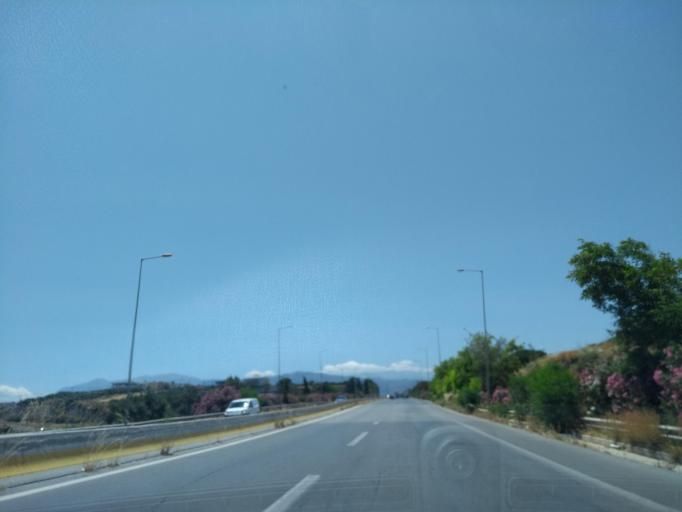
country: GR
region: Crete
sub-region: Nomos Irakleiou
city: Gazi
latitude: 35.3232
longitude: 25.0990
